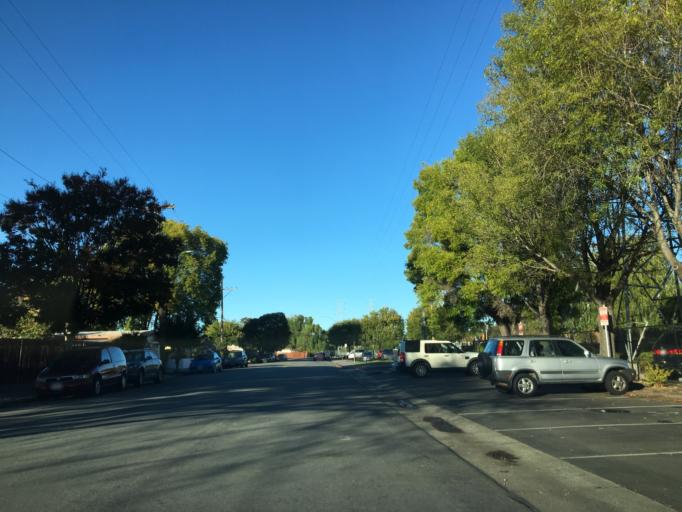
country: US
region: California
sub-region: Santa Clara County
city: Sunnyvale
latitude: 37.3868
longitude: -122.0132
